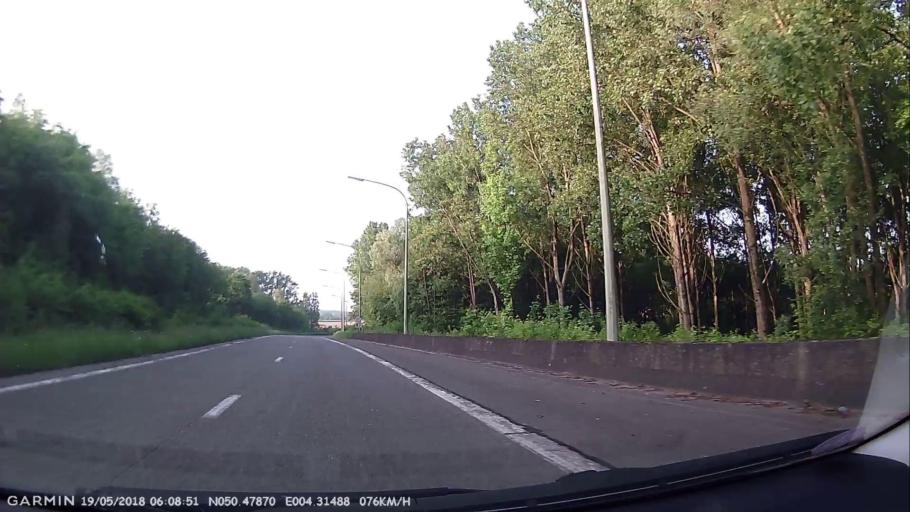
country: BE
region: Wallonia
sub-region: Province du Hainaut
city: Chapelle-lez-Herlaimont
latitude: 50.4785
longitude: 4.3149
